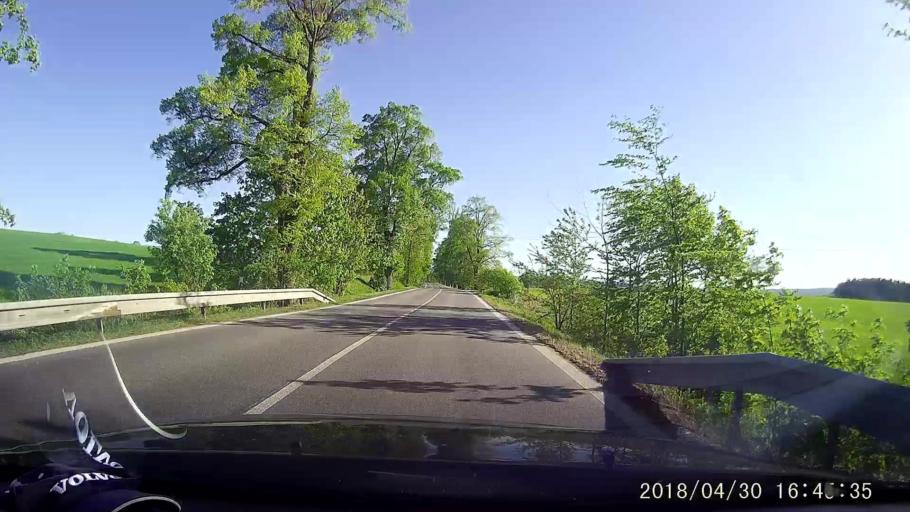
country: PL
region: Silesian Voivodeship
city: Zawidow
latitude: 50.9896
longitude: 15.0777
